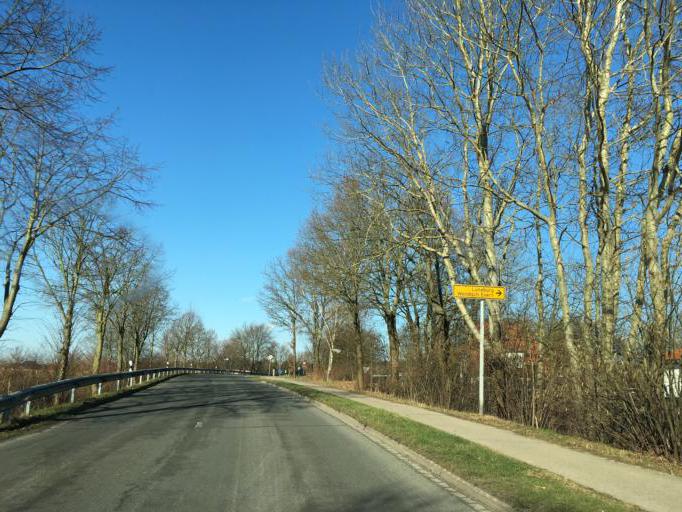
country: DE
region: Lower Saxony
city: Deutsch Evern
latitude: 53.2017
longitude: 10.4324
